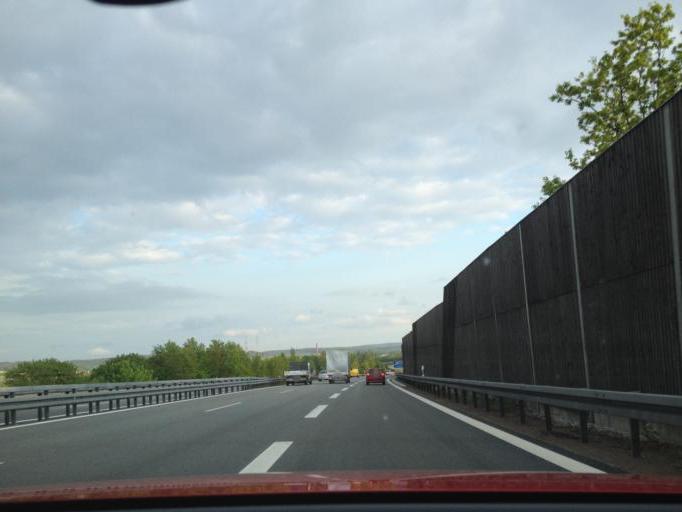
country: DE
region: Bavaria
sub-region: Upper Palatinate
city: Schirmitz
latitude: 49.6539
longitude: 12.1469
